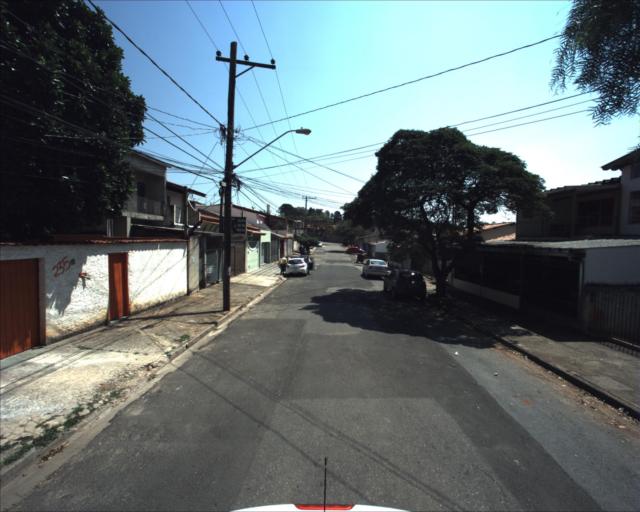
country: BR
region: Sao Paulo
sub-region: Sorocaba
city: Sorocaba
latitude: -23.4600
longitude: -47.4975
